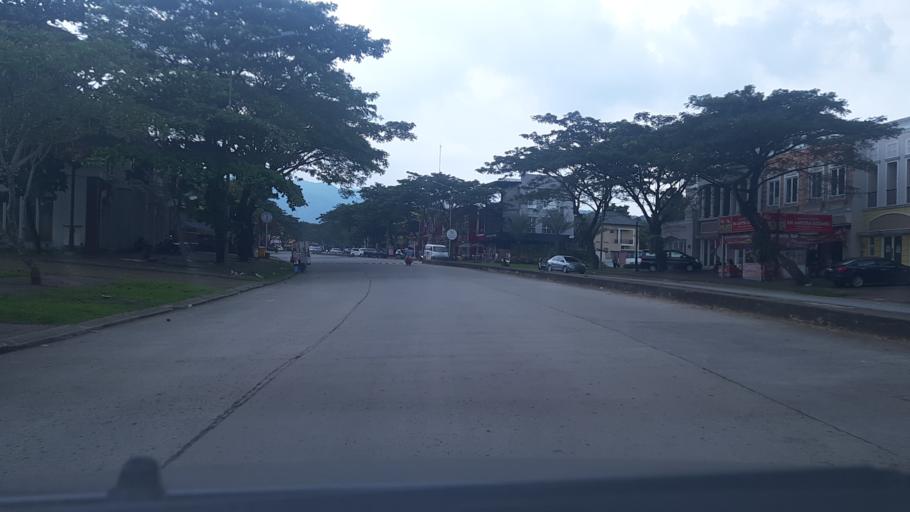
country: ID
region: West Java
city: Citeureup
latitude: -6.5774
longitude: 106.8904
